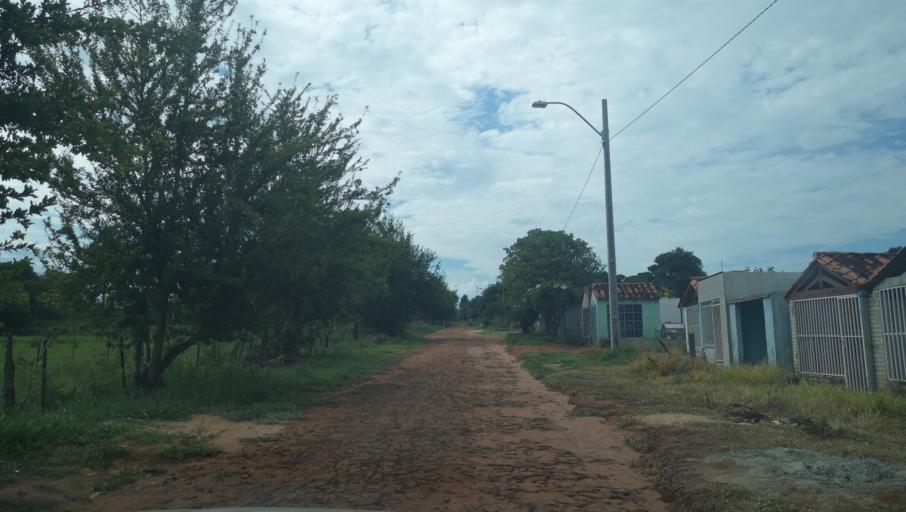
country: PY
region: San Pedro
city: Capiibary
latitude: -24.7187
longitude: -56.0245
